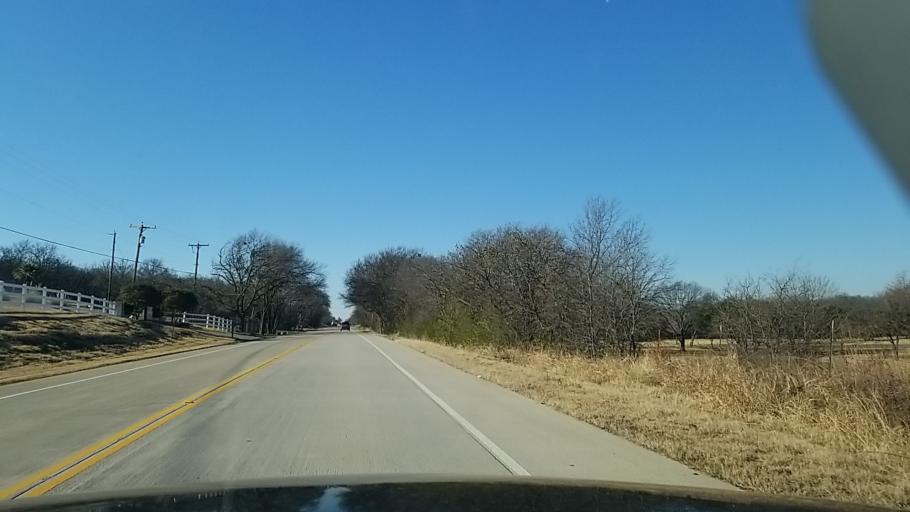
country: US
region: Texas
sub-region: Denton County
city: Argyle
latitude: 33.1367
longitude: -97.1643
